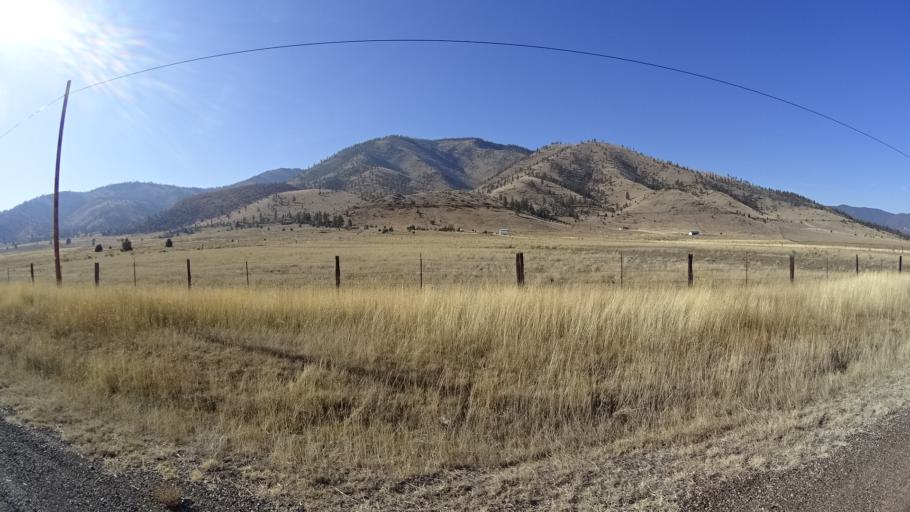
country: US
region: California
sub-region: Siskiyou County
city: Weed
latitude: 41.4825
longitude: -122.4946
